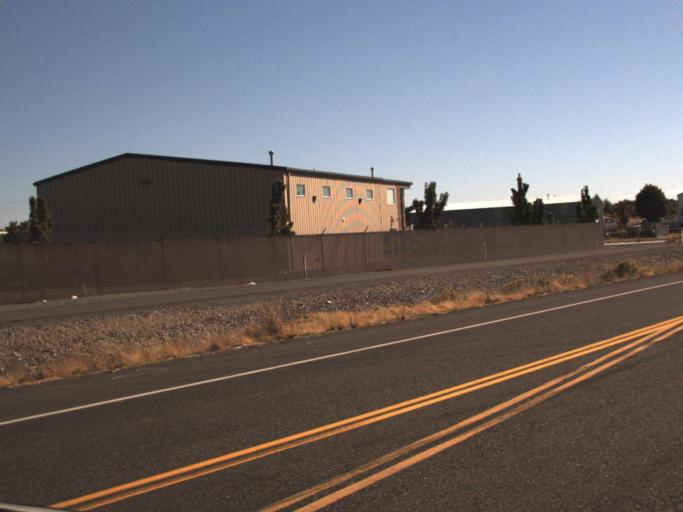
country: US
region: Washington
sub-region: Benton County
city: Richland
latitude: 46.3145
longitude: -119.2945
